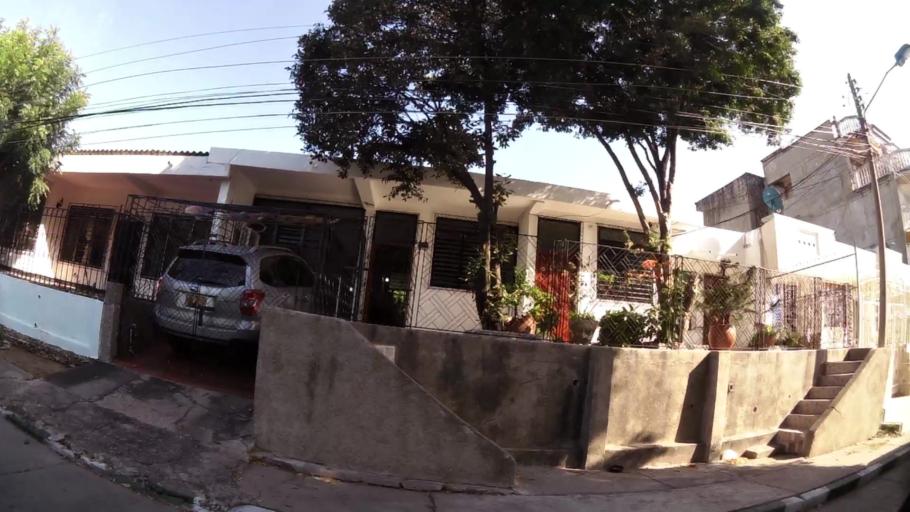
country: CO
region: Bolivar
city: Cartagena
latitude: 10.3890
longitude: -75.5173
